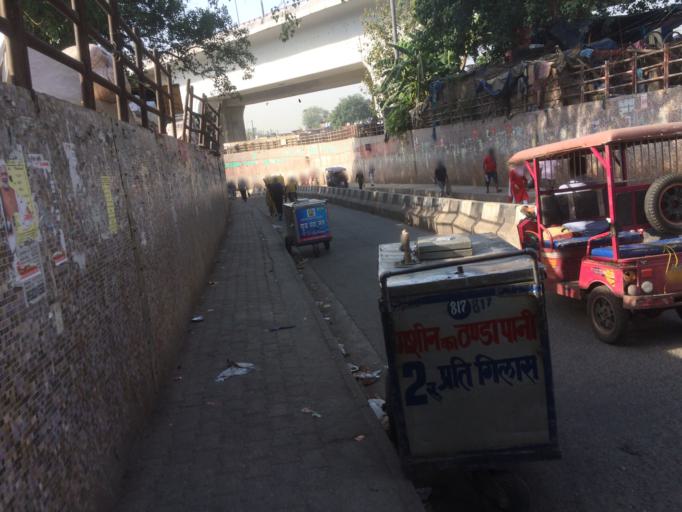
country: IN
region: NCT
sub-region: New Delhi
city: New Delhi
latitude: 28.5850
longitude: 77.2537
